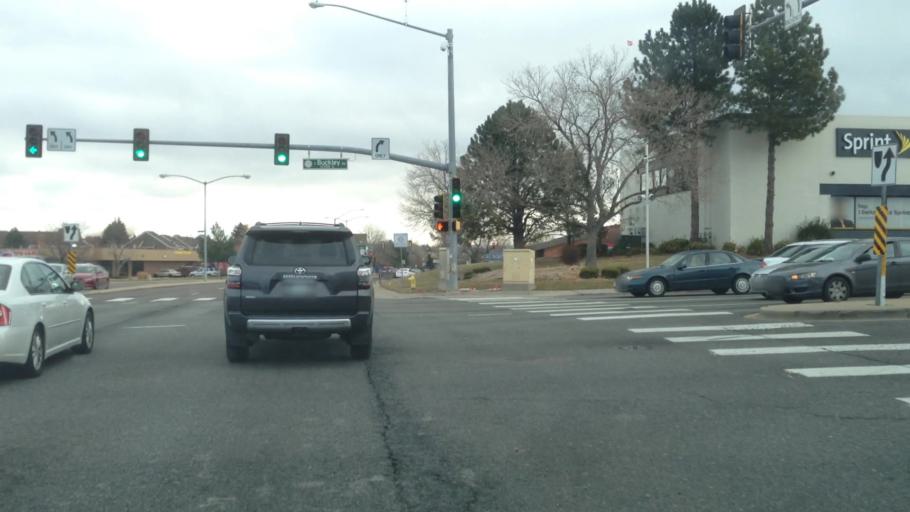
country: US
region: Colorado
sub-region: Adams County
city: Aurora
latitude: 39.6735
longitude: -104.7913
